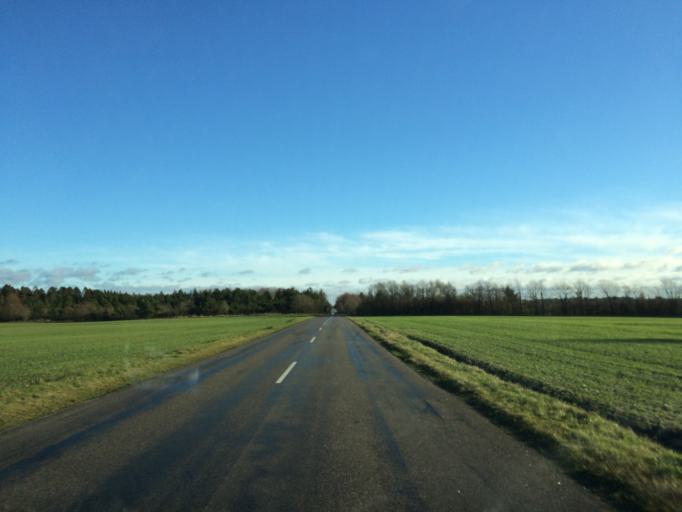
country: DK
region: Central Jutland
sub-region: Herning Kommune
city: Kibaek
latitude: 56.0691
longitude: 8.7476
